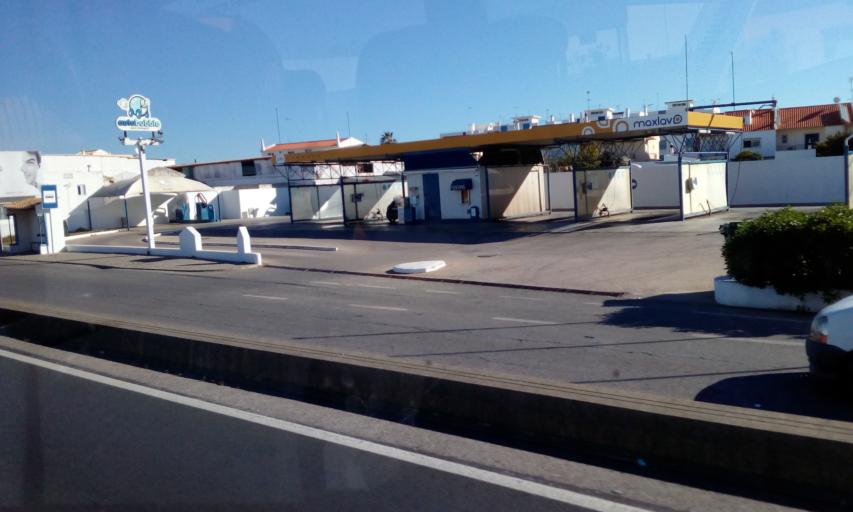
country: PT
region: Faro
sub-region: Faro
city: Faro
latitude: 37.0468
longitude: -7.9528
